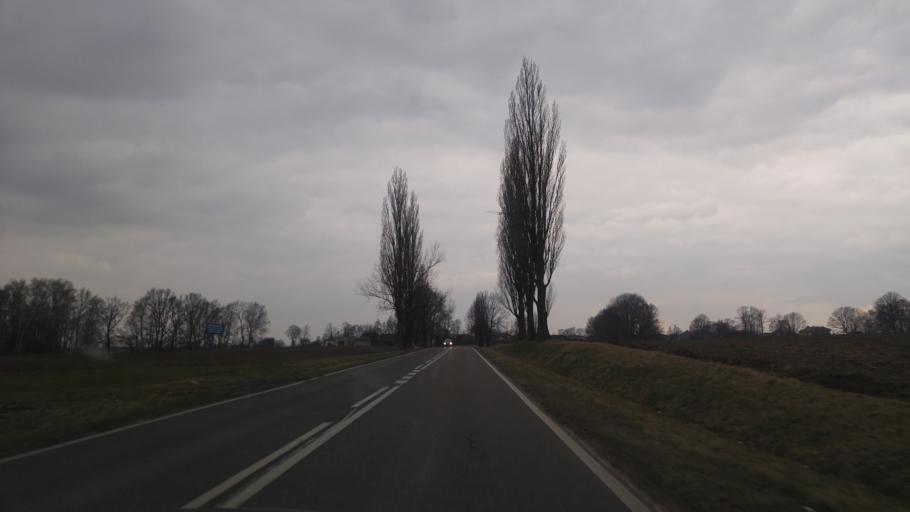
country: PL
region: Silesian Voivodeship
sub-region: Powiat pszczynski
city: Radostowice
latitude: 49.9499
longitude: 18.8612
